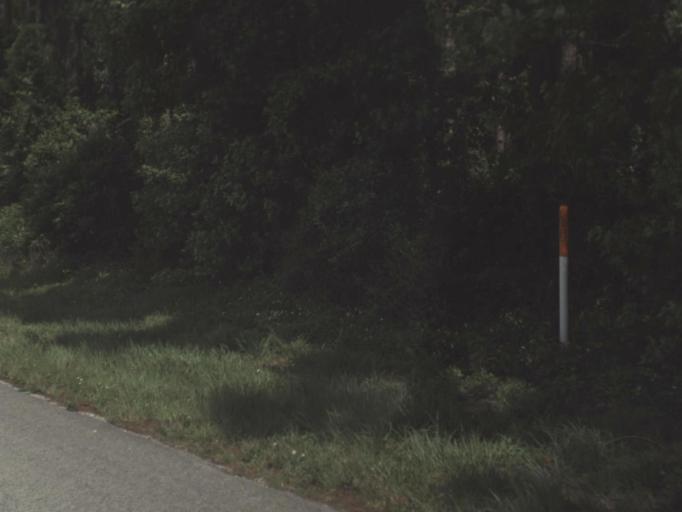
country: US
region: Florida
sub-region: Putnam County
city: East Palatka
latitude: 29.7255
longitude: -81.4678
